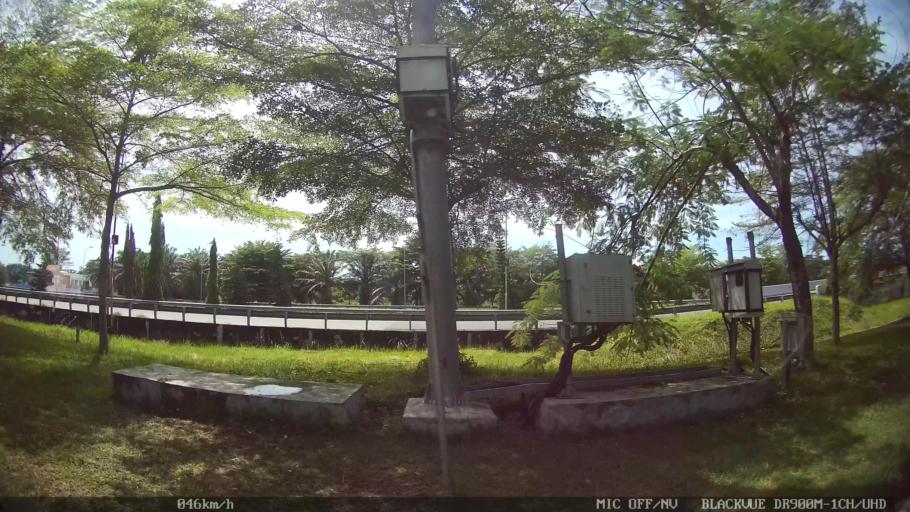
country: ID
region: North Sumatra
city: Percut
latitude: 3.6120
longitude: 98.8551
